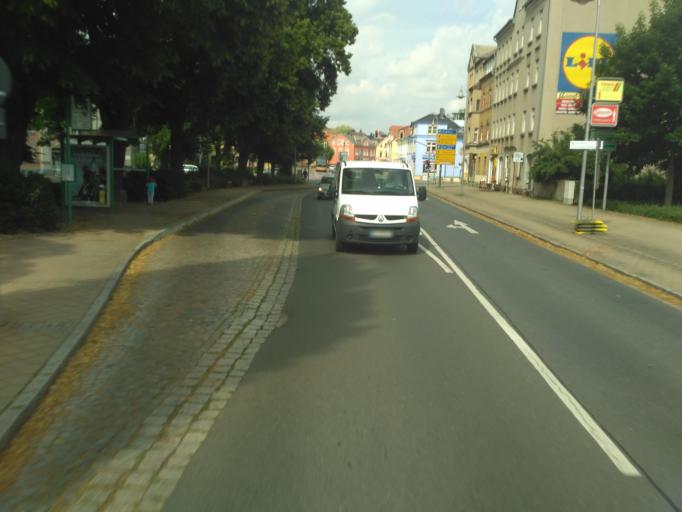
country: DE
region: Saxony
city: Meissen
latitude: 51.1658
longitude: 13.4874
